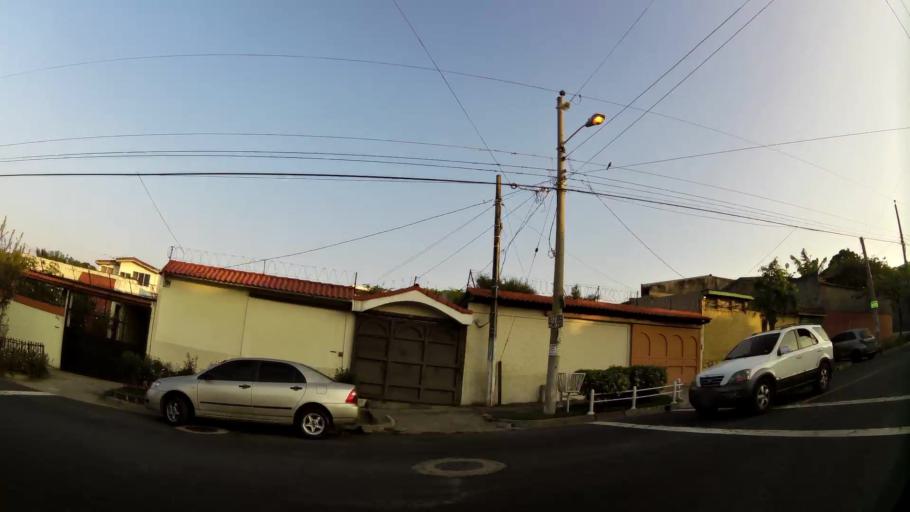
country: SV
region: San Salvador
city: San Salvador
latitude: 13.6832
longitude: -89.2107
